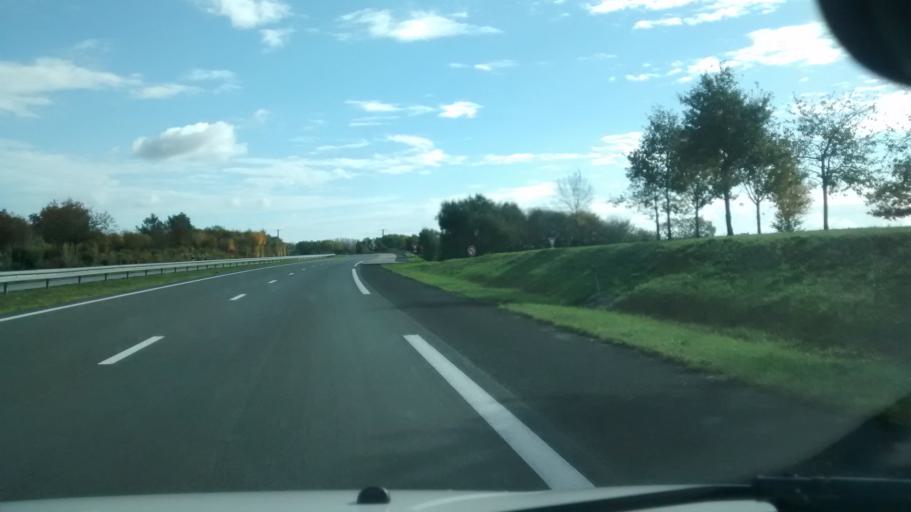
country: FR
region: Pays de la Loire
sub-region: Departement de Maine-et-Loire
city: Pouance
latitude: 47.7594
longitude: -1.1917
